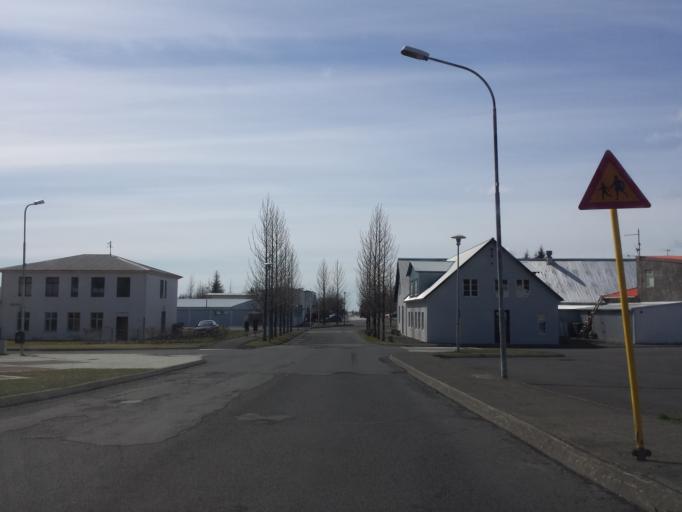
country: IS
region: South
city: Hveragerdi
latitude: 64.0016
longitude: -21.1842
